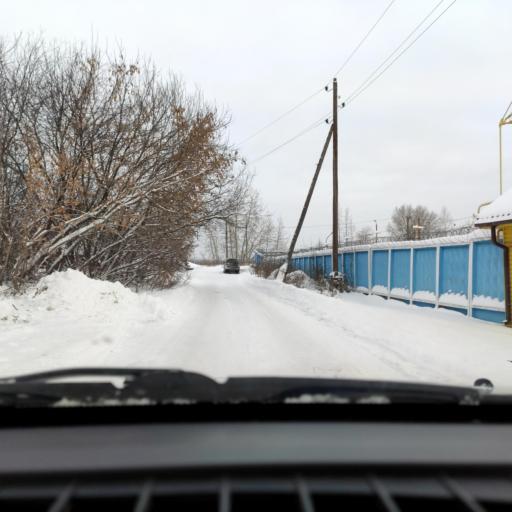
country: RU
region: Perm
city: Kondratovo
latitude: 58.0086
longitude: 56.1216
